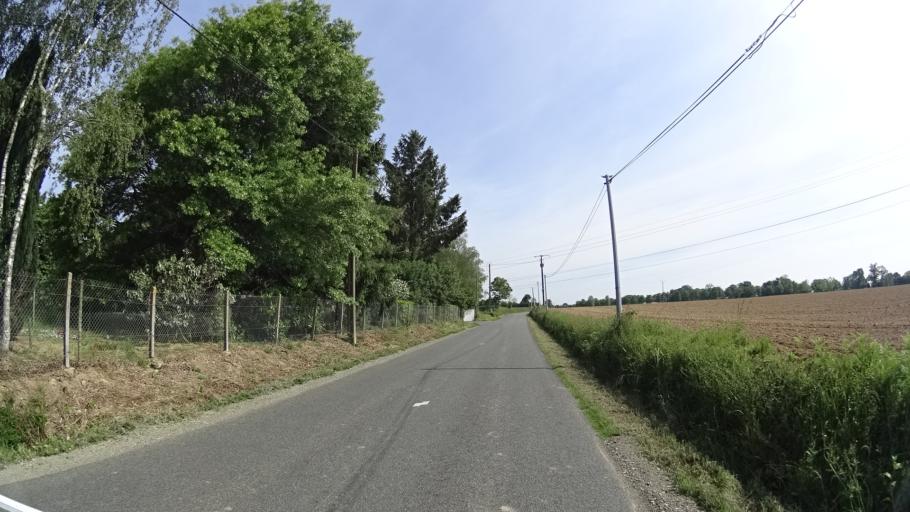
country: FR
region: Brittany
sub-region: Departement d'Ille-et-Vilaine
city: Nouvoitou
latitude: 48.0281
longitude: -1.5341
